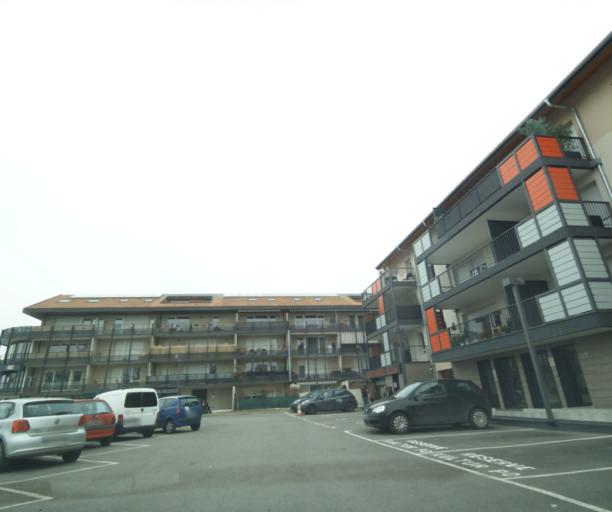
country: FR
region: Rhone-Alpes
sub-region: Departement de la Haute-Savoie
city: Reignier-Esery
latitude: 46.1385
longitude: 6.2709
